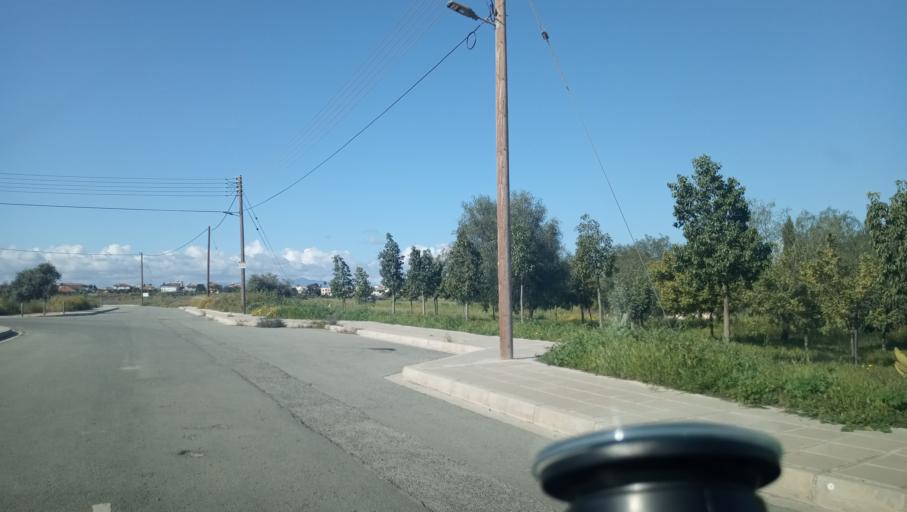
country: CY
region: Lefkosia
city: Geri
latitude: 35.1040
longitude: 33.3980
